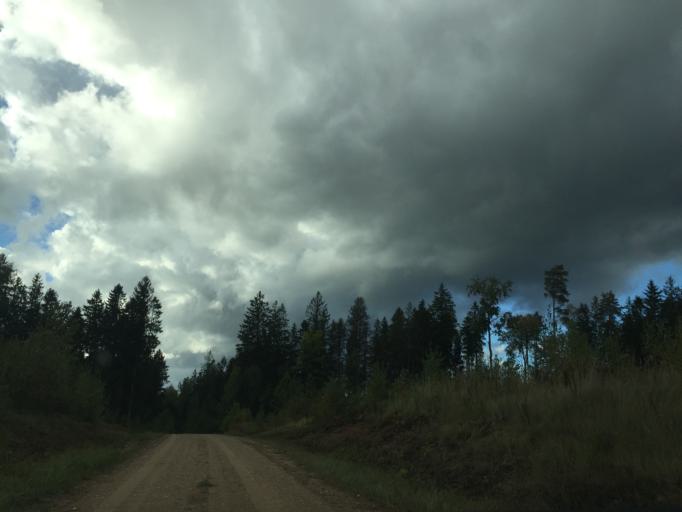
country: LV
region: Ligatne
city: Ligatne
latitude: 57.1021
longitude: 25.1469
